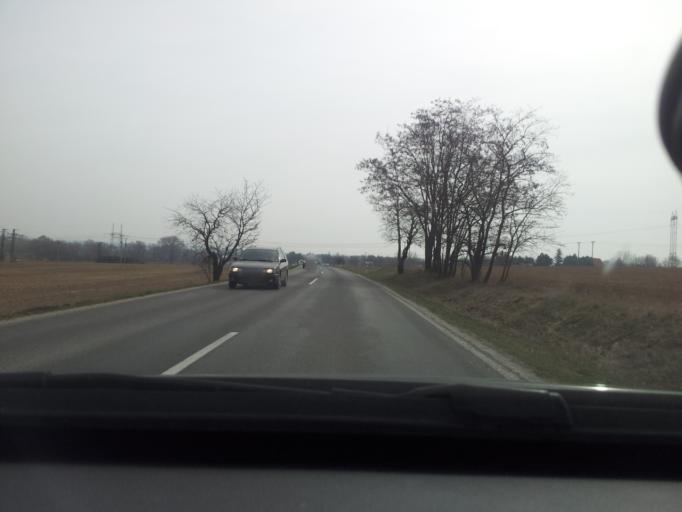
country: SK
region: Trnavsky
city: Hlohovec
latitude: 48.3771
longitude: 17.8781
